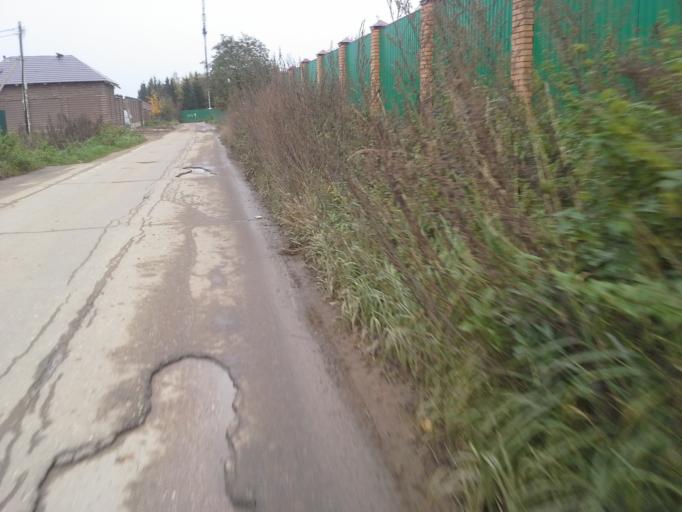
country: RU
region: Moskovskaya
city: Nazar'yevo
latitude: 55.6841
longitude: 37.0151
